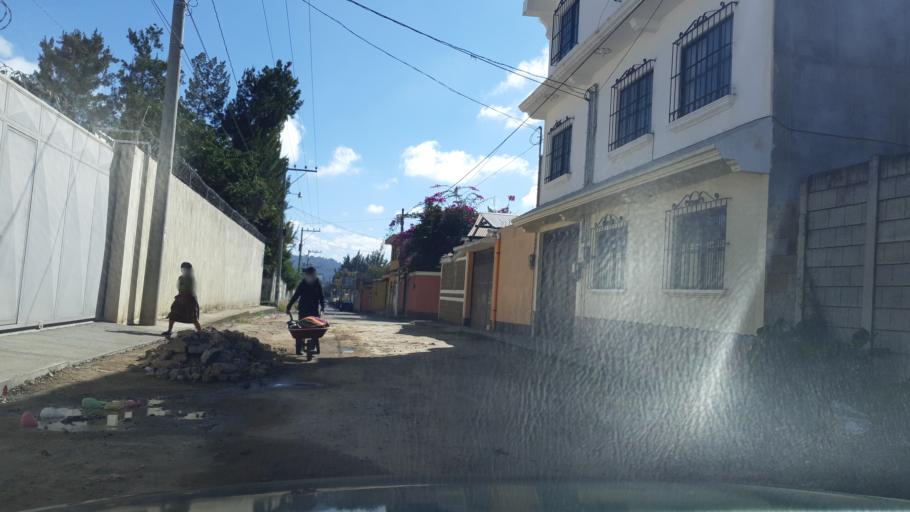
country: GT
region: Chimaltenango
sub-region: Municipio de Chimaltenango
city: Chimaltenango
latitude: 14.6529
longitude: -90.8183
